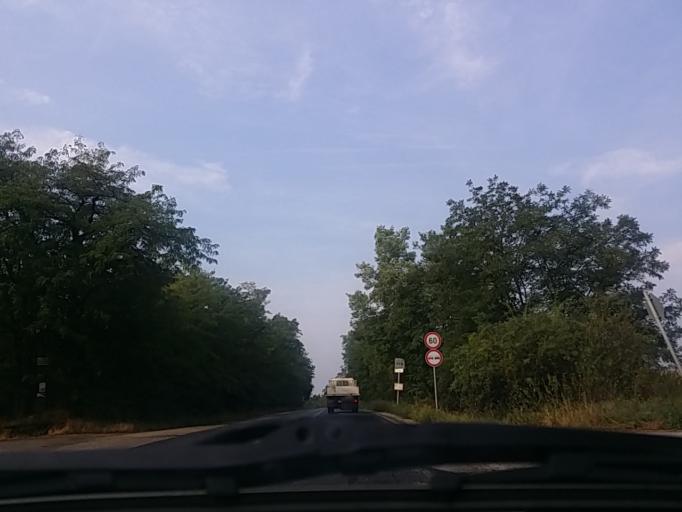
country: HU
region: Fejer
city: Many
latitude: 47.5154
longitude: 18.6455
